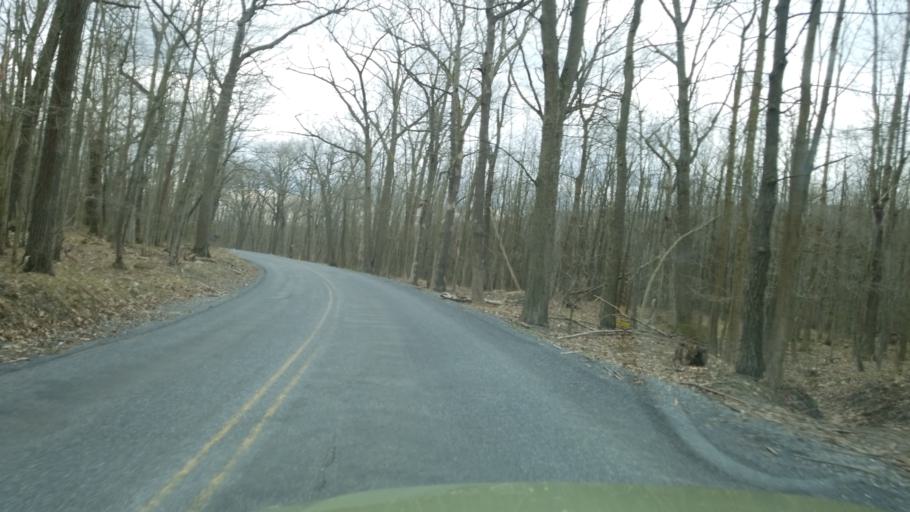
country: US
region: Pennsylvania
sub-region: Blair County
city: Tipton
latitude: 40.7233
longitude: -78.3539
